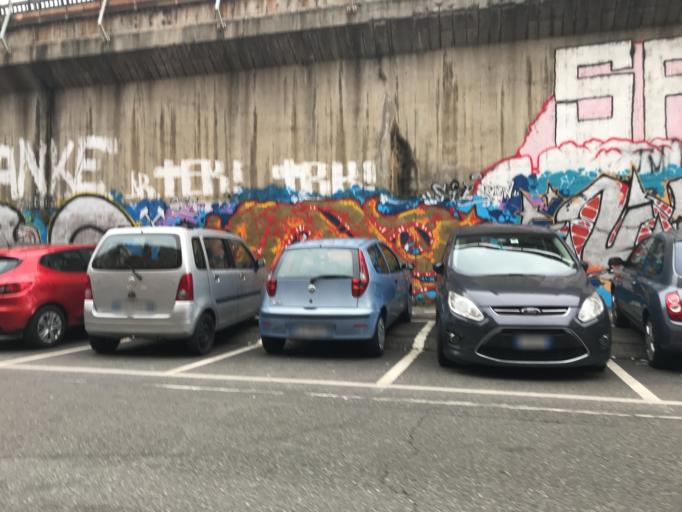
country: IT
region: Lombardy
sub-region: Citta metropolitana di Milano
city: Sesto San Giovanni
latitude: 45.4917
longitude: 9.2316
